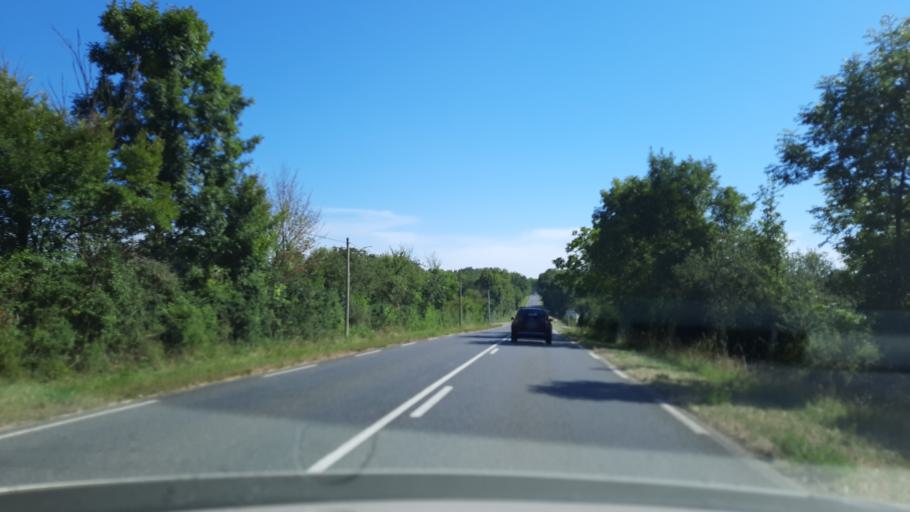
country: FR
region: Midi-Pyrenees
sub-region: Departement du Tarn-et-Garonne
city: Caylus
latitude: 44.3095
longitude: 1.8845
